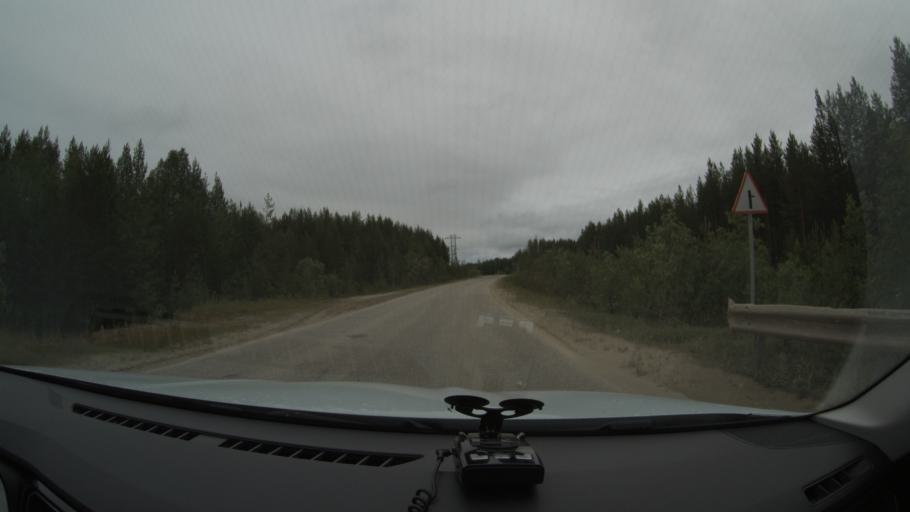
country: RU
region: Komi Republic
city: Kozhva
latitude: 65.1146
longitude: 56.9999
